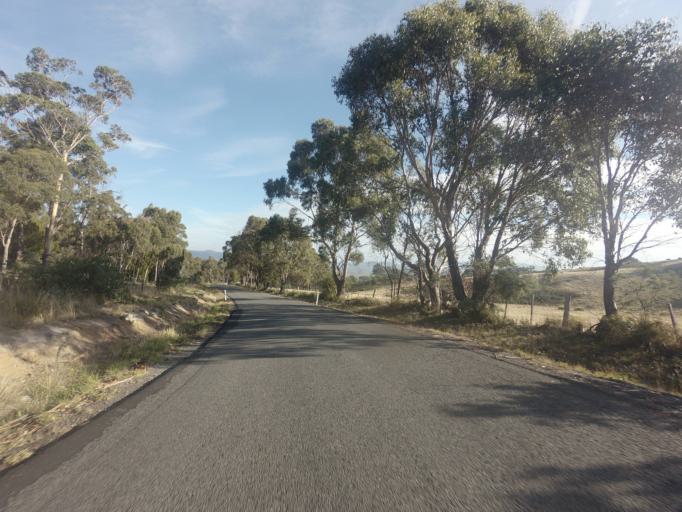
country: AU
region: Tasmania
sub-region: Brighton
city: Bridgewater
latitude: -42.5159
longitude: 147.3855
